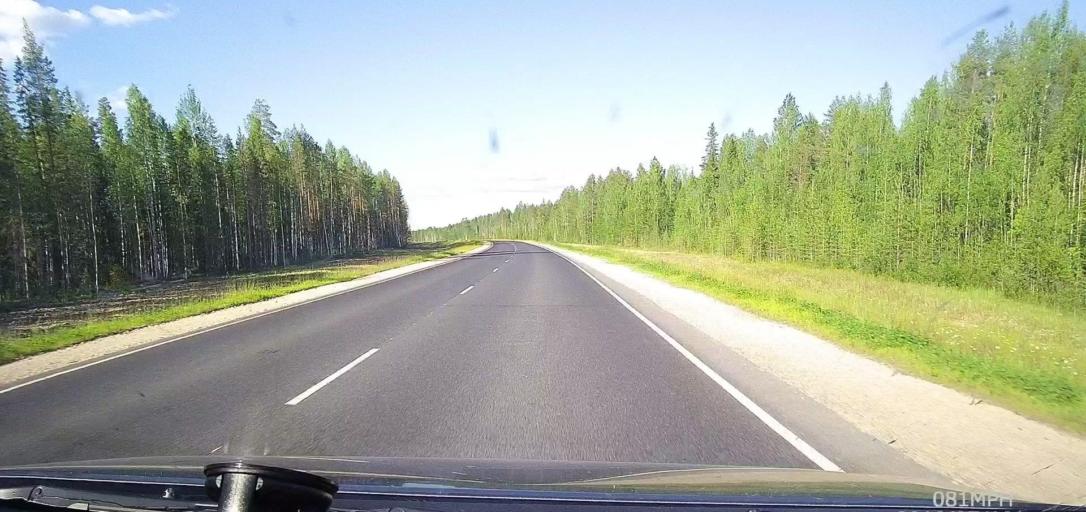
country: RU
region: Arkhangelskaya
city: Yemtsa
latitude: 63.1538
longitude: 40.5173
